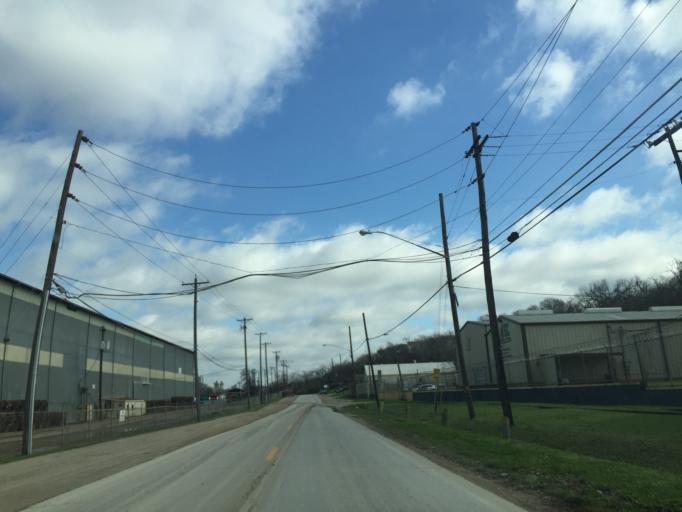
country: US
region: Texas
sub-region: Dallas County
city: Dallas
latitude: 32.7727
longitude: -96.8443
